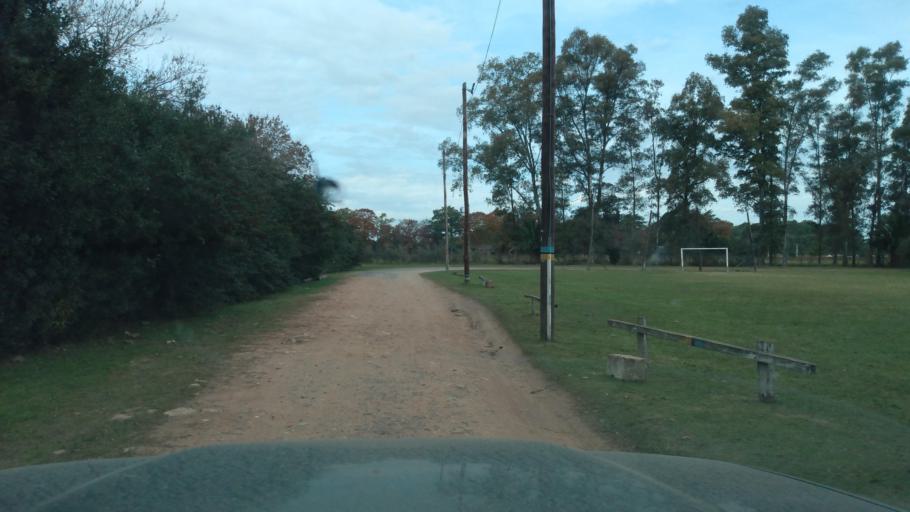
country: AR
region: Buenos Aires
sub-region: Partido de Lujan
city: Lujan
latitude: -34.5934
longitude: -59.1846
